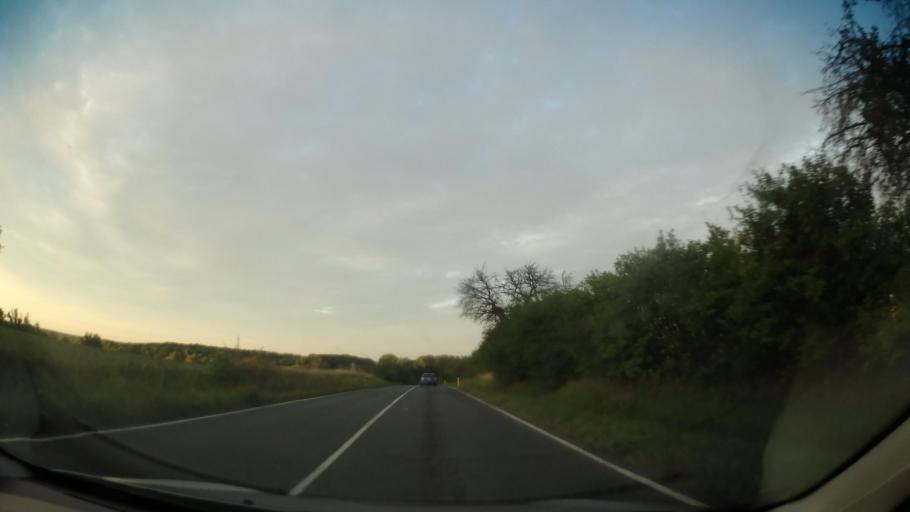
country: CZ
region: Central Bohemia
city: Milovice
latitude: 50.2145
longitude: 14.8634
